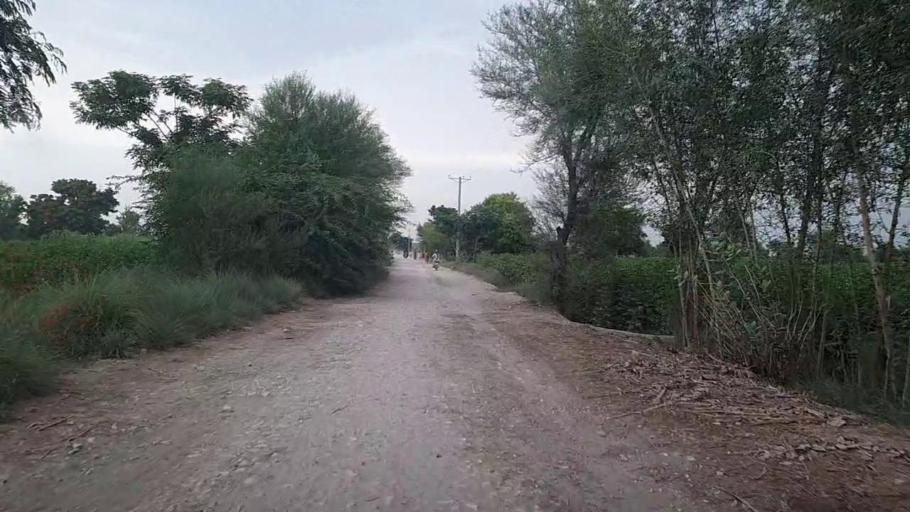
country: PK
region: Sindh
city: Karaundi
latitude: 26.9780
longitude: 68.3438
